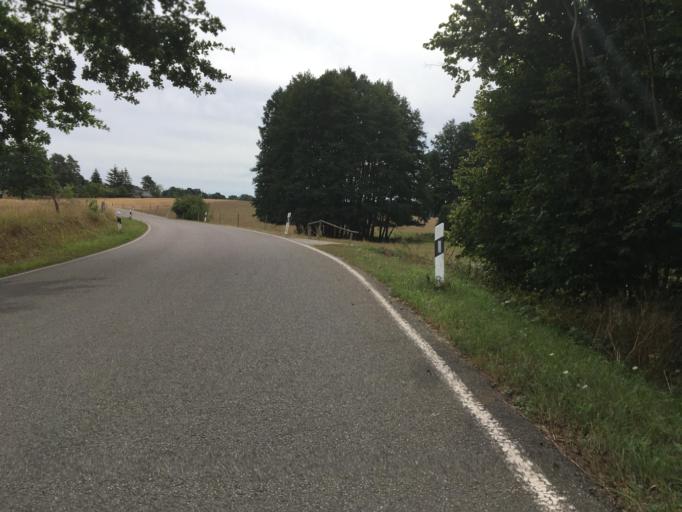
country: DE
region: Brandenburg
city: Milmersdorf
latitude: 53.1152
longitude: 13.6655
